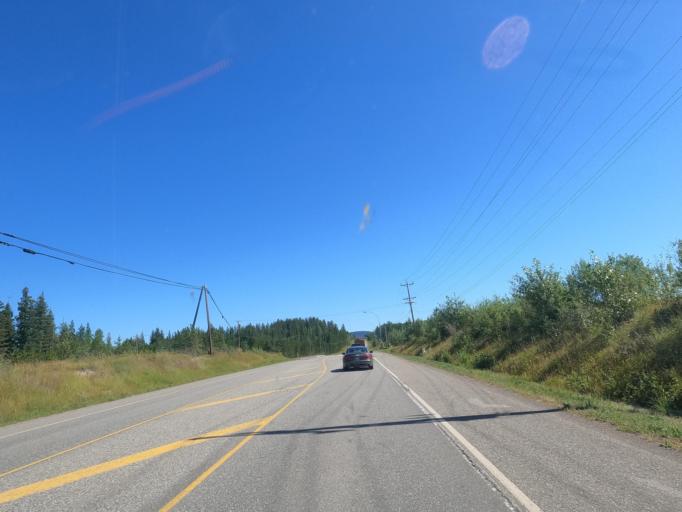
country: CA
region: British Columbia
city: Quesnel
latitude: 53.0706
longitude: -122.4263
